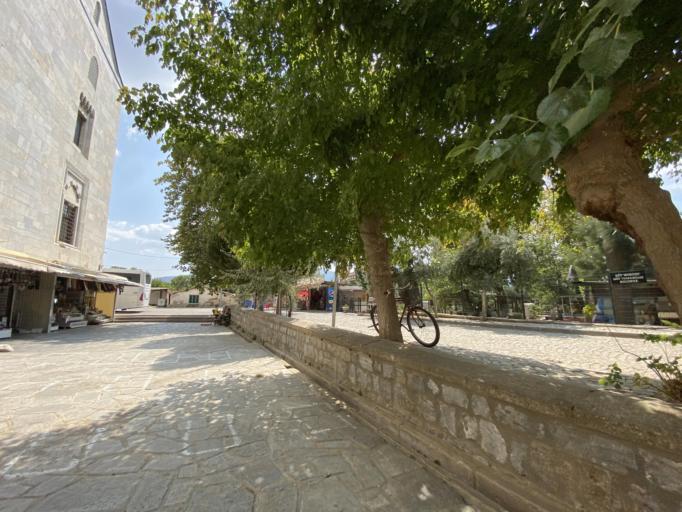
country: TR
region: Izmir
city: Selcuk
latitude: 37.9523
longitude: 27.3656
